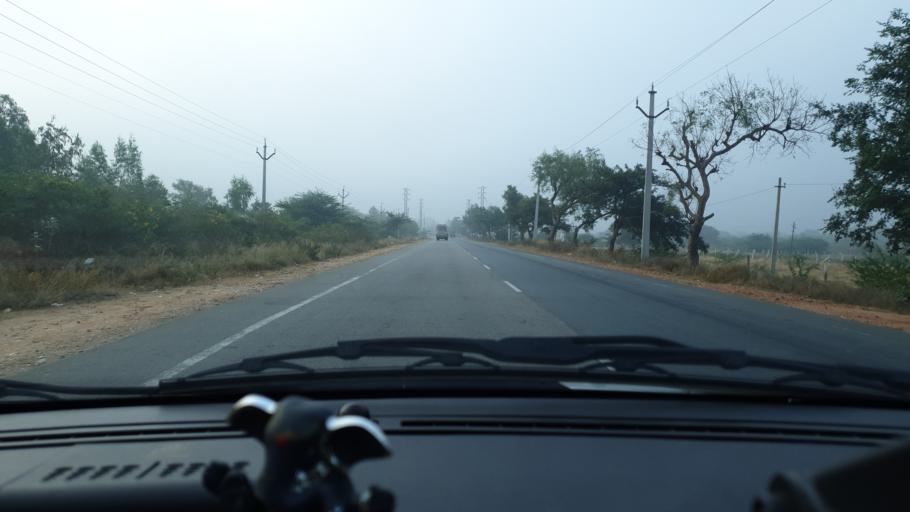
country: IN
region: Telangana
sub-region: Mahbubnagar
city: Farrukhnagar
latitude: 16.8896
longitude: 78.5297
